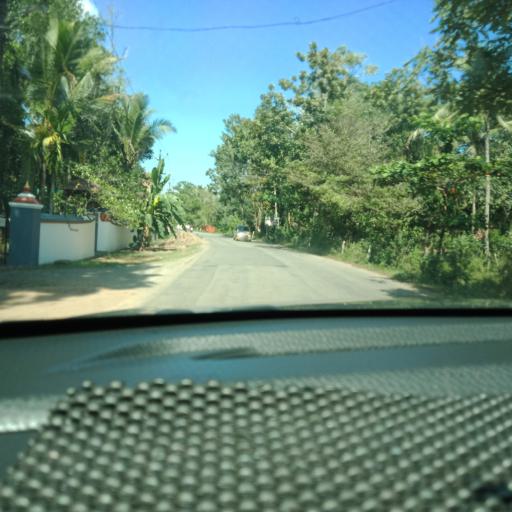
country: IN
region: Kerala
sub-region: Alappuzha
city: Mavelikara
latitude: 9.3020
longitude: 76.4560
